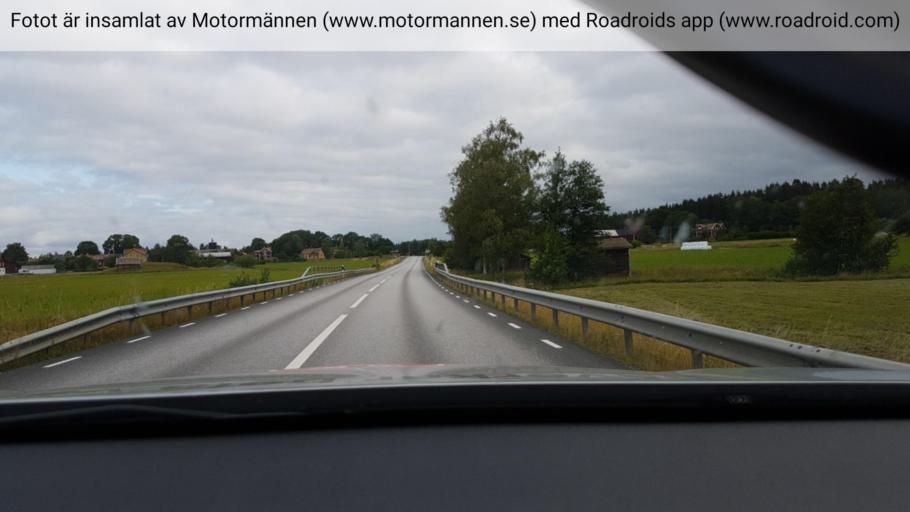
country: SE
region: Stockholm
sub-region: Norrtalje Kommun
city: Skanninge
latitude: 59.8381
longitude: 18.4416
